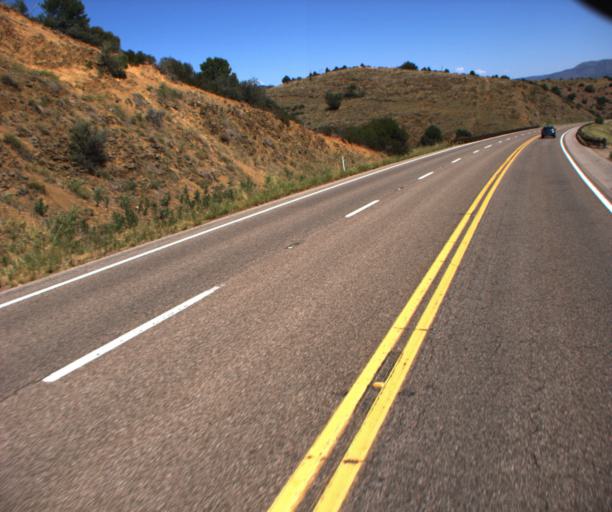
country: US
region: Arizona
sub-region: Gila County
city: Globe
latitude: 33.5196
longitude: -110.7008
